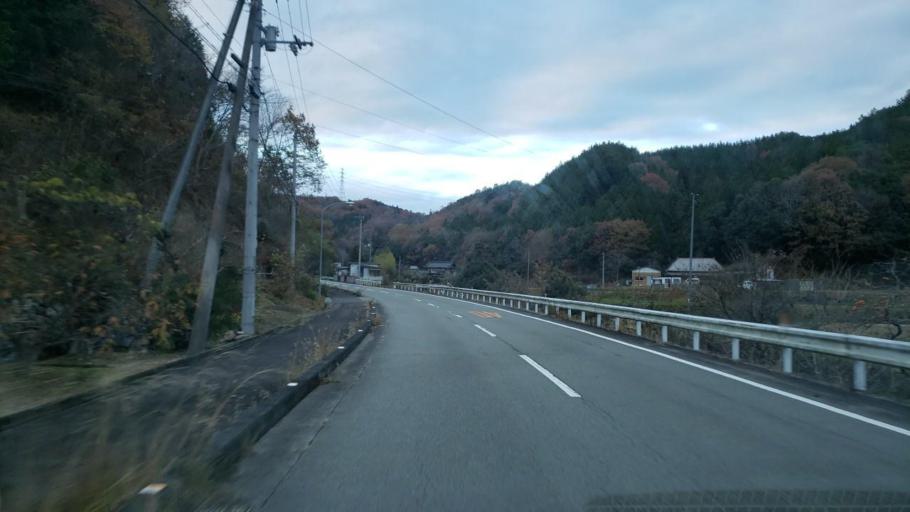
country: JP
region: Tokushima
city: Kamojimacho-jogejima
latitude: 34.1880
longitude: 134.2512
